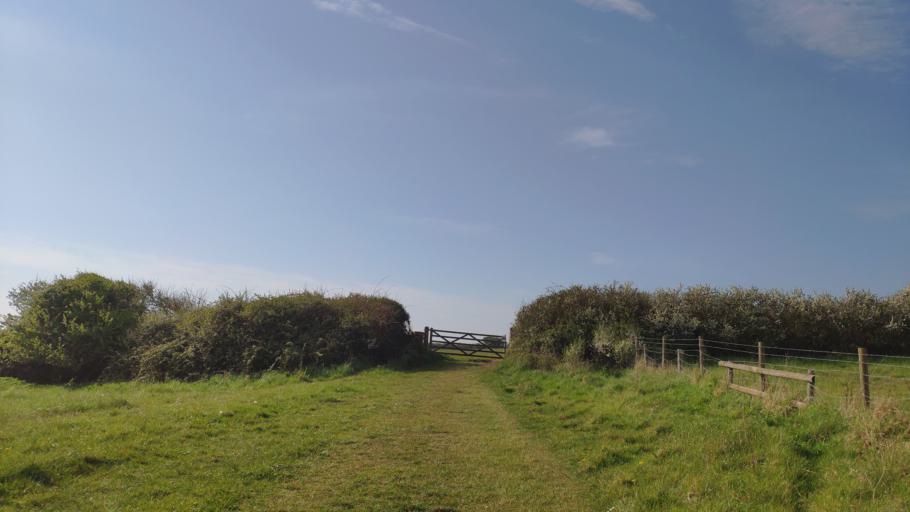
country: GB
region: England
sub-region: Dorset
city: Swanage
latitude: 50.5979
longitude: -1.9667
